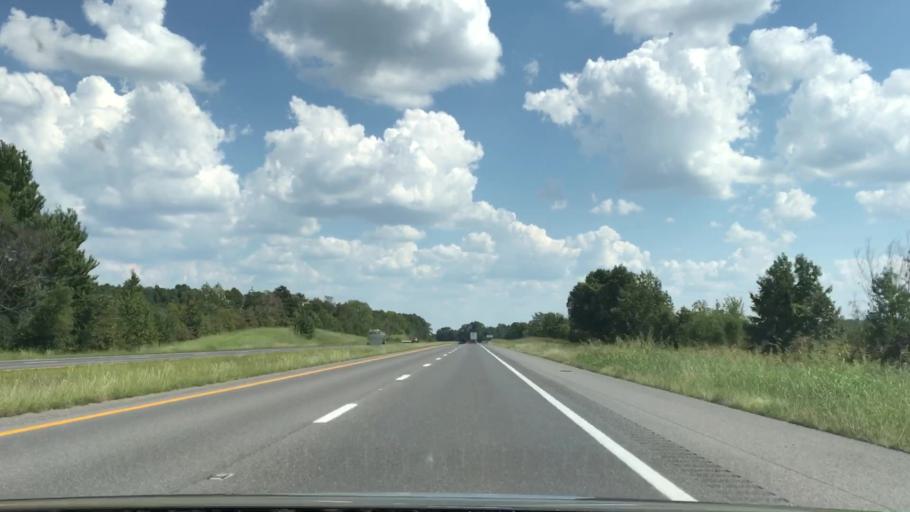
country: US
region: Kentucky
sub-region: Lyon County
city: Eddyville
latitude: 37.1077
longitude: -87.9962
